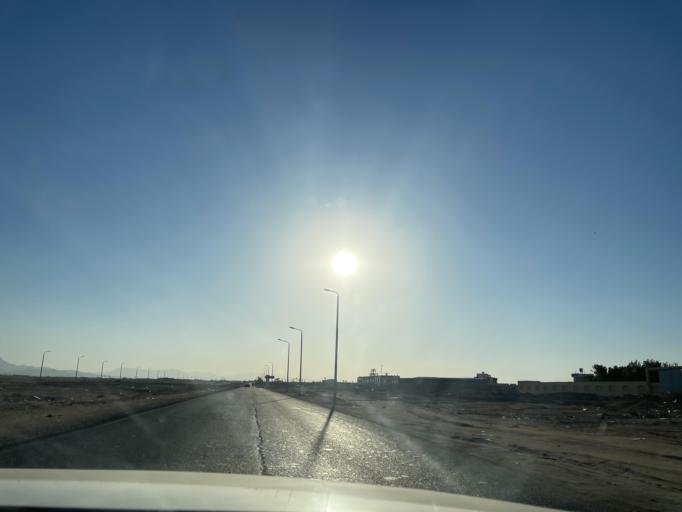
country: EG
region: Red Sea
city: Hurghada
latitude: 27.2170
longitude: 33.8024
